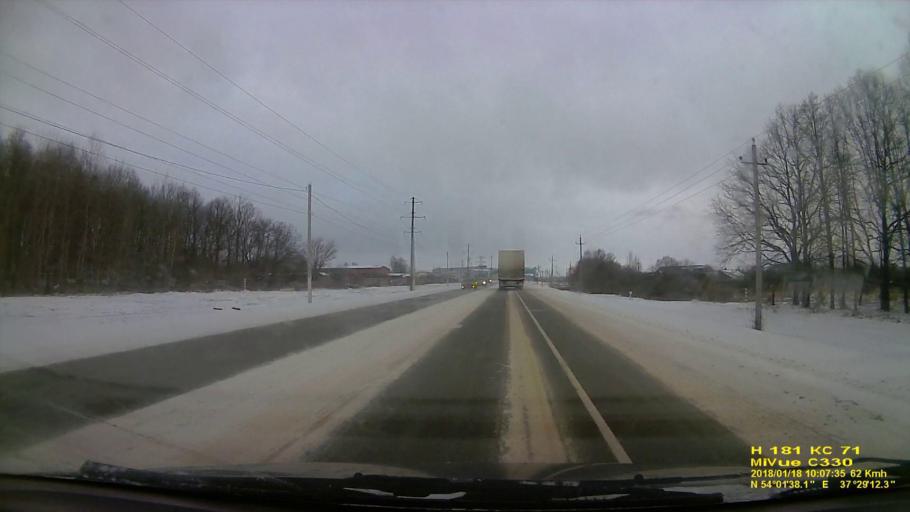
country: RU
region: Tula
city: Pervomayskiy
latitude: 54.0270
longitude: 37.4867
